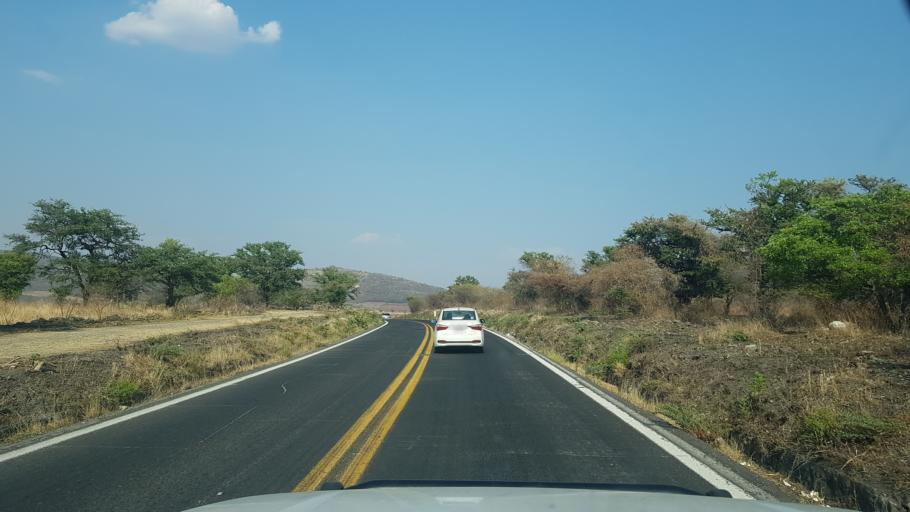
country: MX
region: Puebla
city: Calmeca
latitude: 18.6546
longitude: -98.6536
